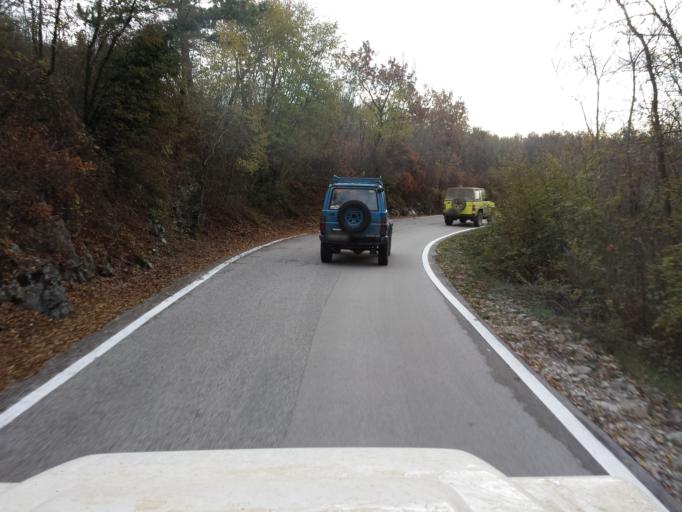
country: IT
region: Friuli Venezia Giulia
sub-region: Provincia di Gorizia
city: Farra d'Isonzo
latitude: 45.8818
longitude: 13.5373
